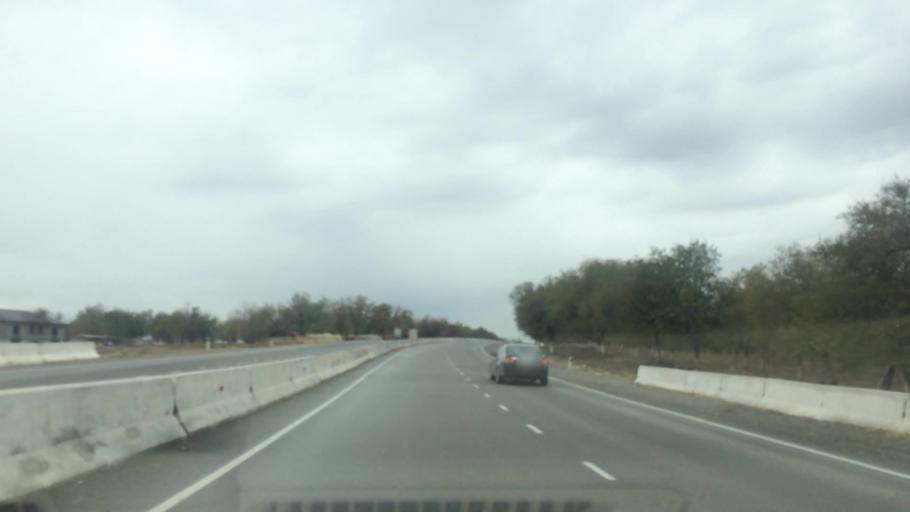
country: UZ
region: Samarqand
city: Bulung'ur
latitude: 39.9194
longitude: 67.5155
